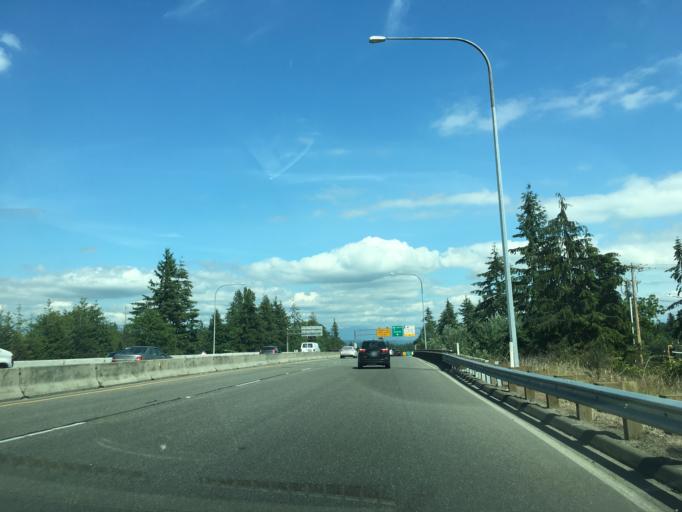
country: US
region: Washington
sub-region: Snohomish County
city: Everett
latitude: 47.9226
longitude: -122.2238
